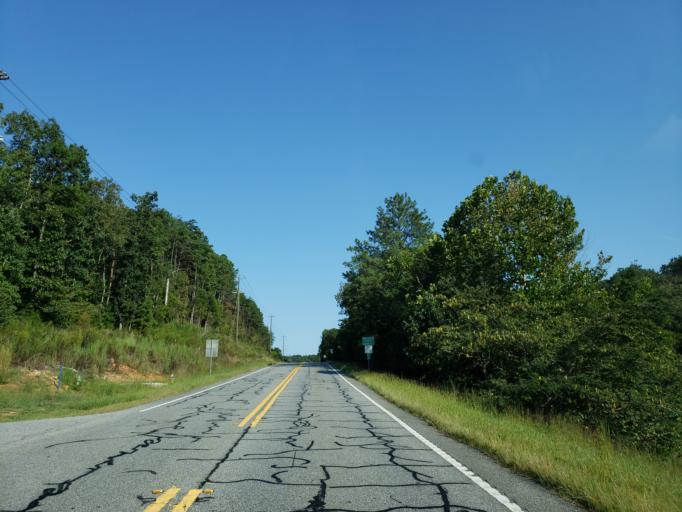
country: US
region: Georgia
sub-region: Whitfield County
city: Varnell
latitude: 34.9020
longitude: -85.0156
